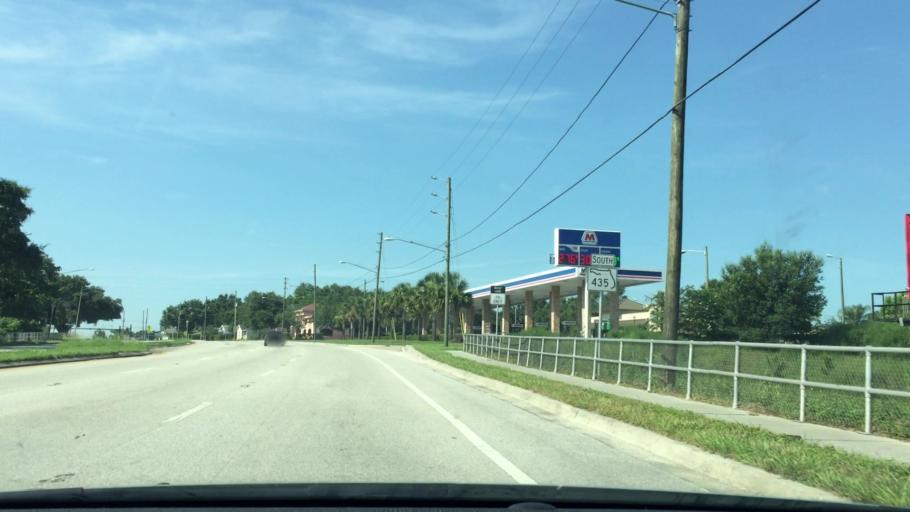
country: US
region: Florida
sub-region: Orange County
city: Orlovista
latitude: 28.5465
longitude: -81.4581
